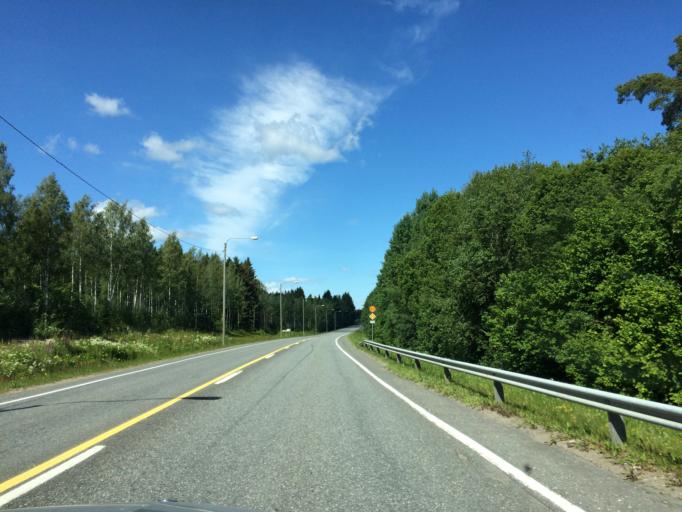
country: FI
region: Haeme
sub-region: Haemeenlinna
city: Haemeenlinna
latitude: 60.9562
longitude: 24.4916
